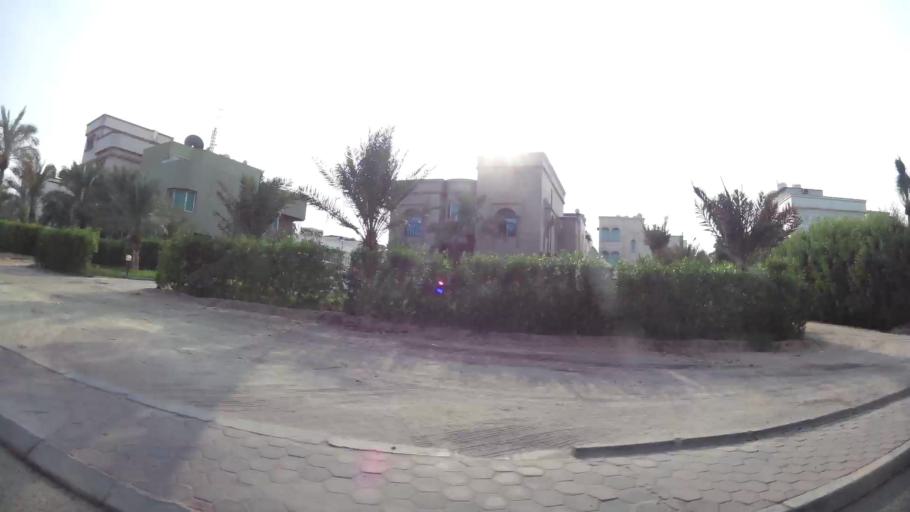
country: KW
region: Mubarak al Kabir
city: Mubarak al Kabir
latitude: 29.2144
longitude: 48.0650
